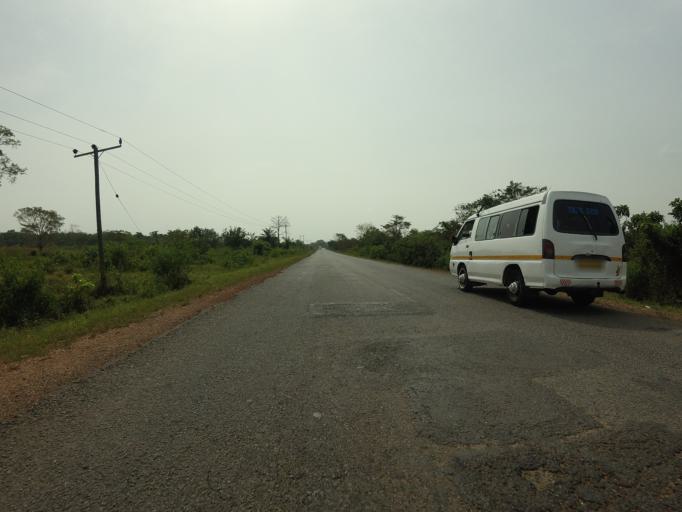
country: GH
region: Volta
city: Ho
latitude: 6.3940
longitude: 0.1809
